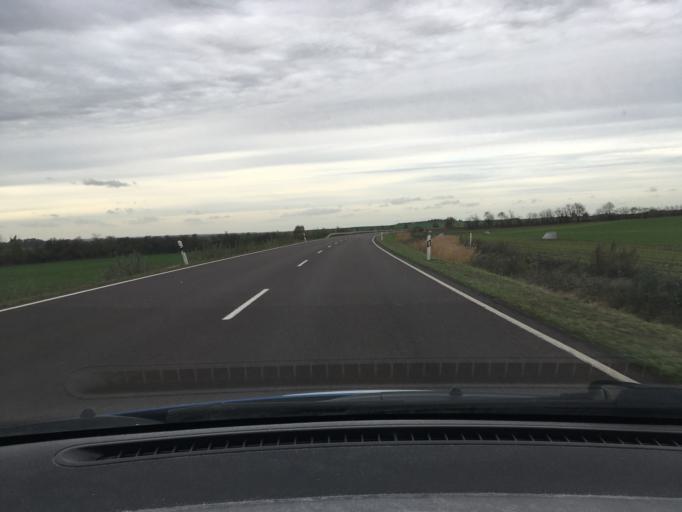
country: DE
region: Saxony-Anhalt
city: Leitzkau
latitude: 52.0519
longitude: 11.9442
